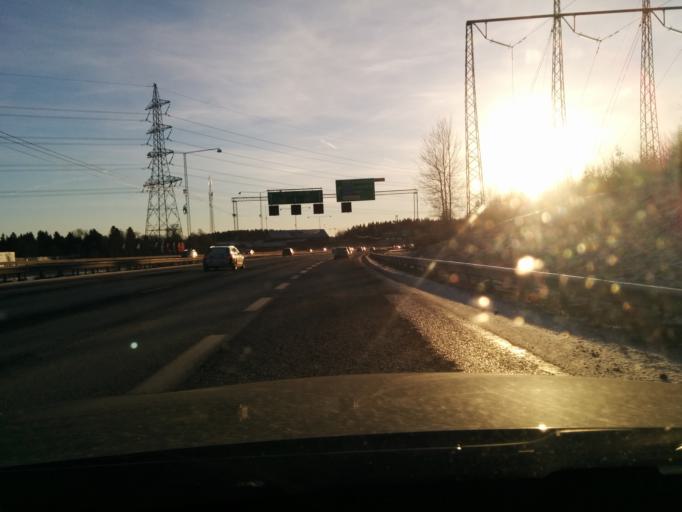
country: SE
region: Stockholm
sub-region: Sollentuna Kommun
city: Sollentuna
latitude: 59.4394
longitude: 17.9237
